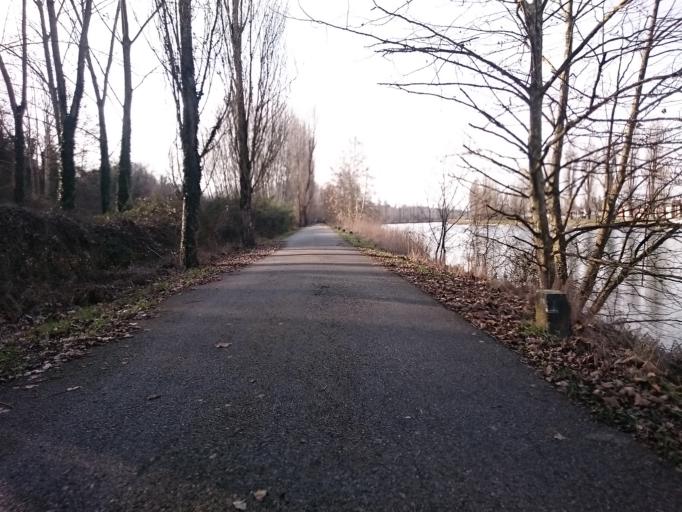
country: IT
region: Veneto
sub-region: Provincia di Verona
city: Salionze
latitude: 45.4188
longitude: 10.7086
